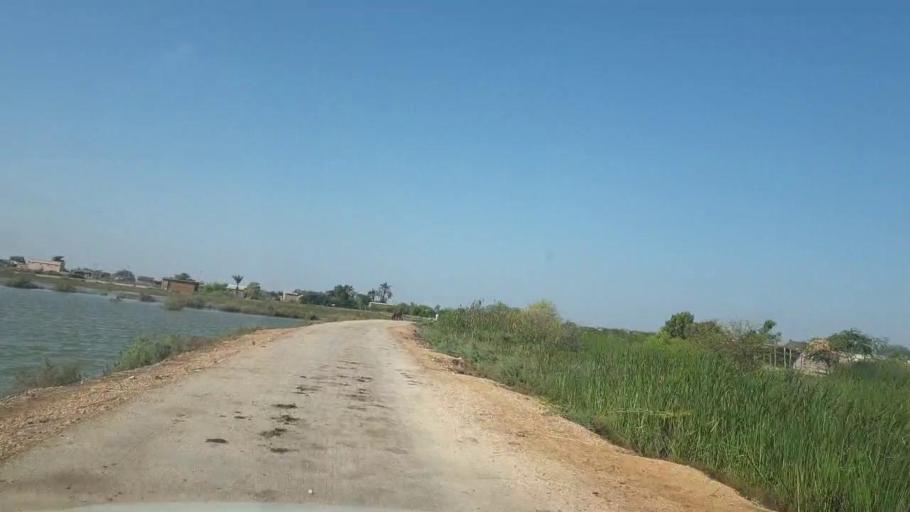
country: PK
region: Sindh
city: Chuhar Jamali
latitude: 24.4644
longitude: 67.8645
